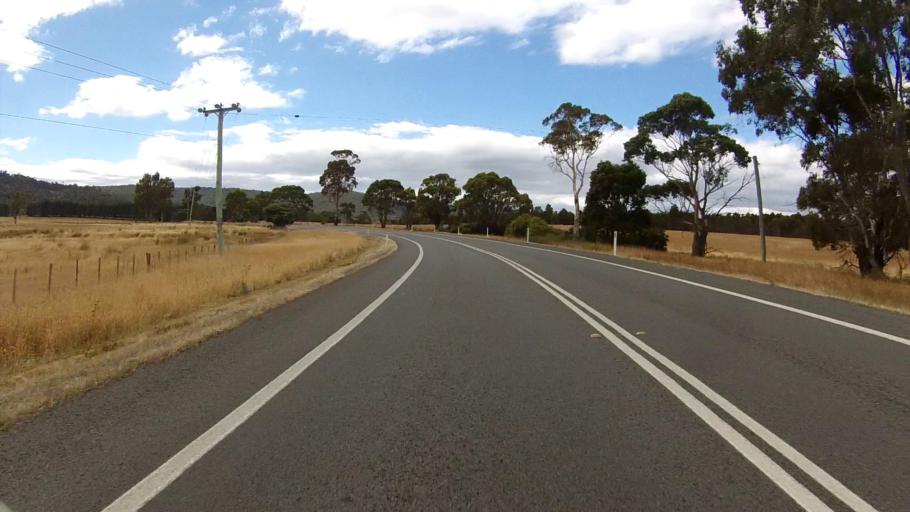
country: AU
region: Tasmania
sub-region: Sorell
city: Sorell
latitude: -42.6397
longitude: 147.5857
